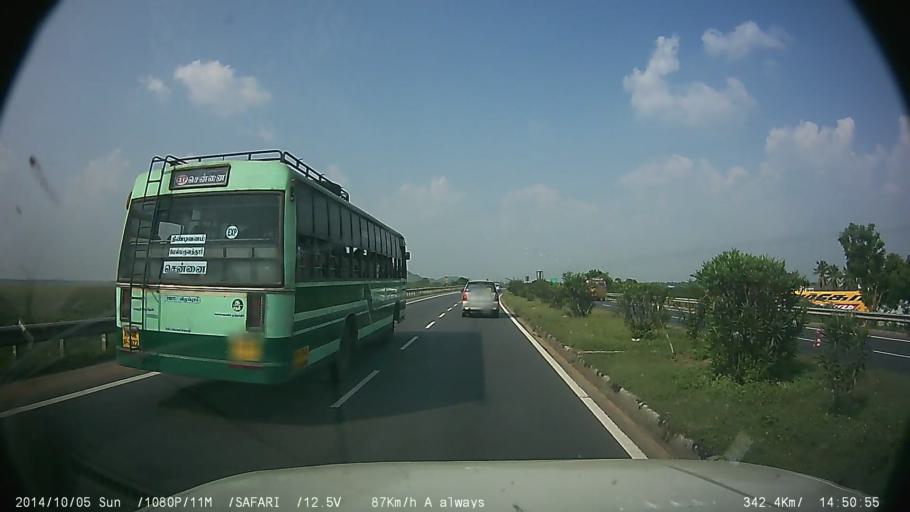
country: IN
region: Tamil Nadu
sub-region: Kancheepuram
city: Madurantakam
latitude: 12.5120
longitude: 79.8835
